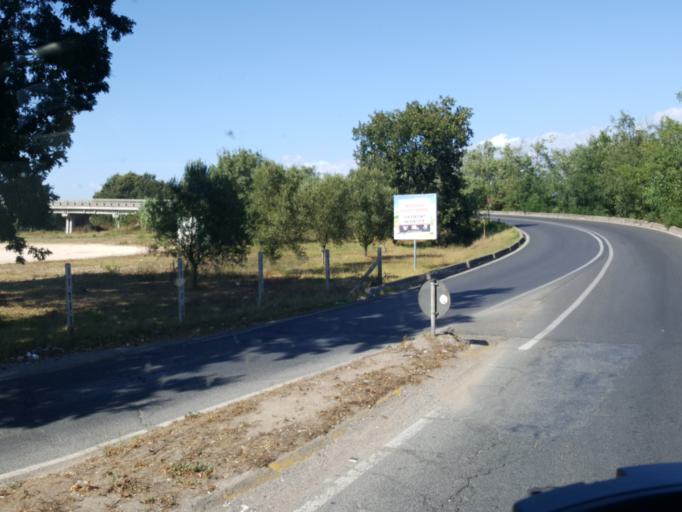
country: IT
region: Latium
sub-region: Citta metropolitana di Roma Capitale
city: Anzio
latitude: 41.5135
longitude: 12.6310
